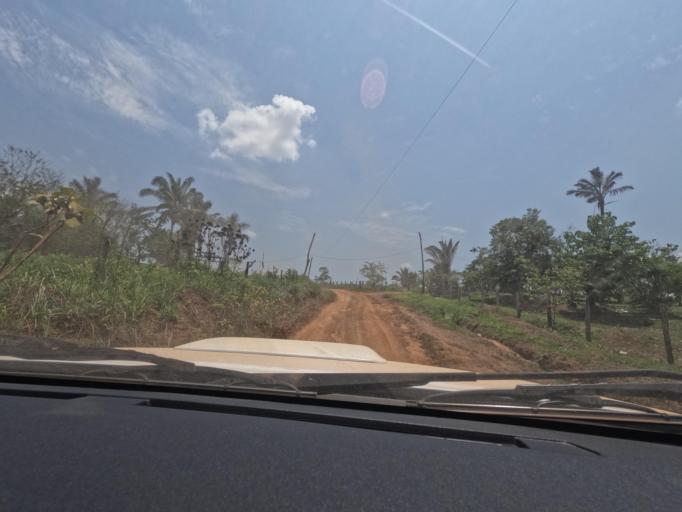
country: BR
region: Rondonia
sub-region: Porto Velho
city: Porto Velho
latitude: -8.6511
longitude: -64.1682
